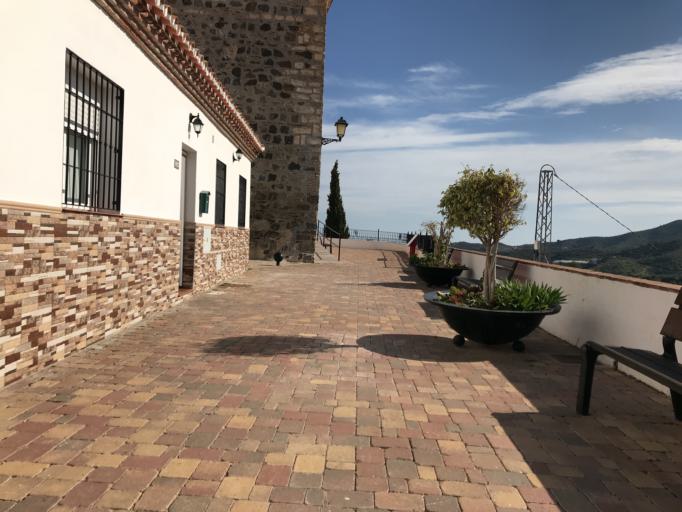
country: ES
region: Andalusia
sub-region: Provincia de Malaga
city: Valdes
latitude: 36.7695
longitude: -4.2165
